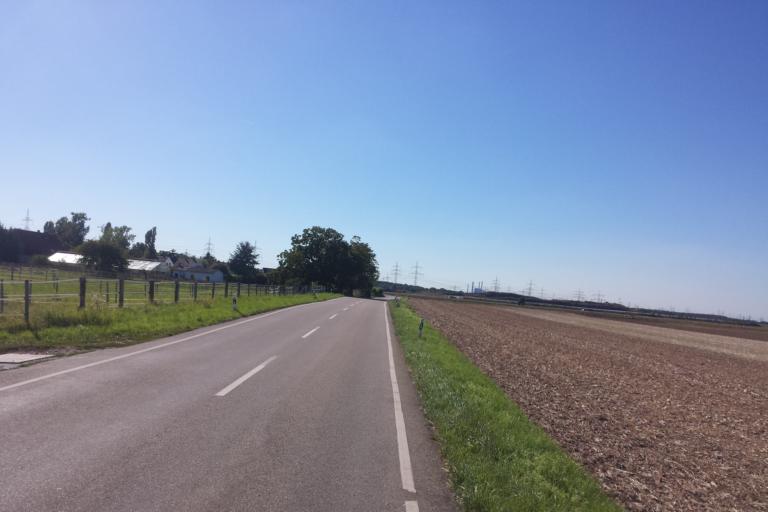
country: DE
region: Baden-Wuerttemberg
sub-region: Karlsruhe Region
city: Plankstadt
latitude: 49.4197
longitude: 8.5999
